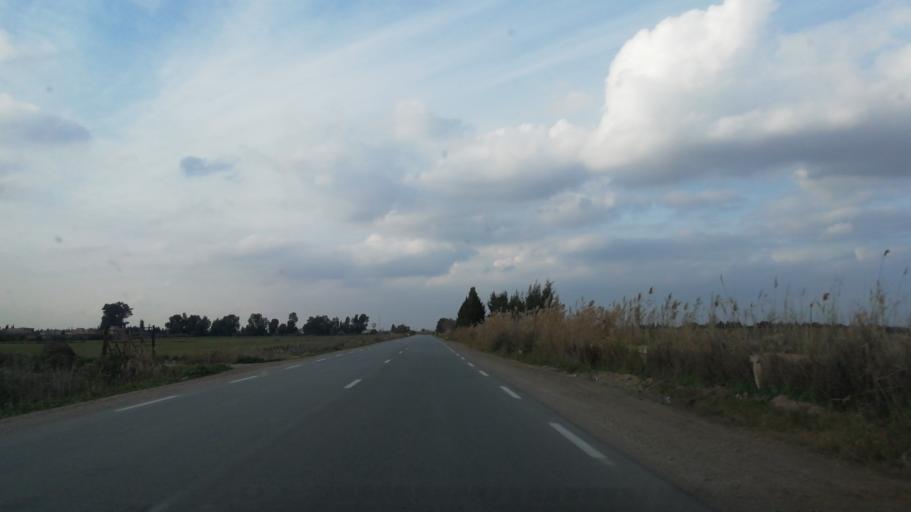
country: DZ
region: Mascara
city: Sig
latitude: 35.6457
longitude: 0.0271
